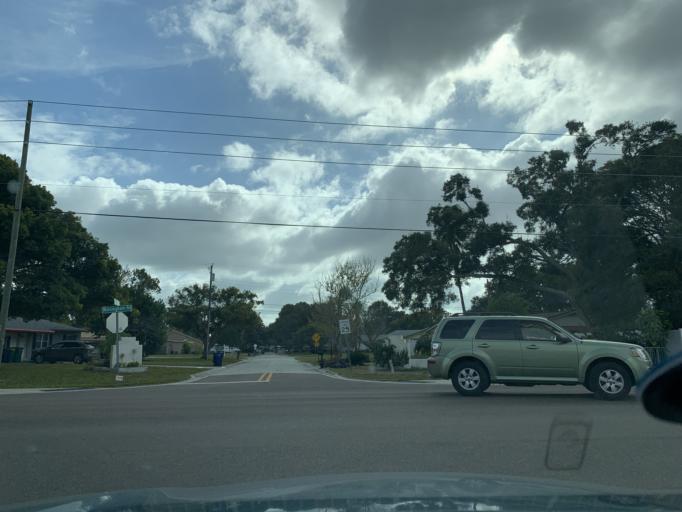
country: US
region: Florida
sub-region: Pinellas County
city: Ridgecrest
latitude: 27.8802
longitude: -82.7899
